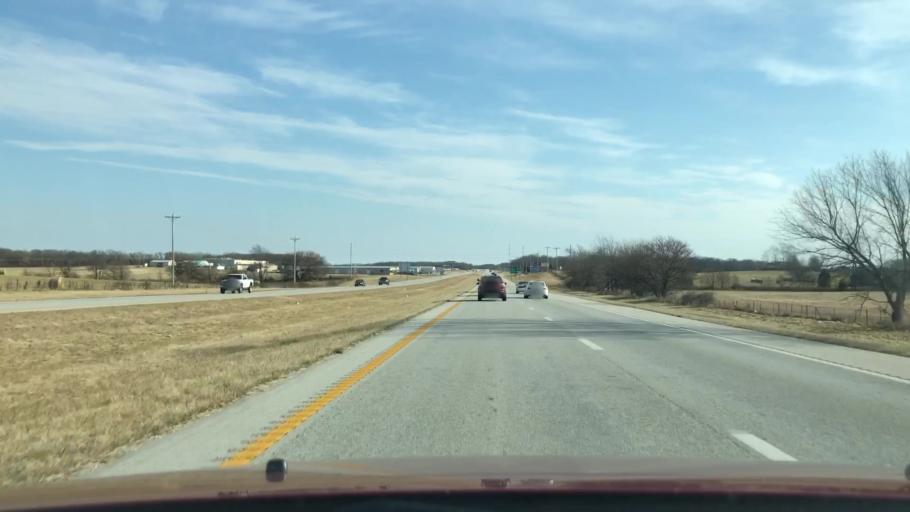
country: US
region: Missouri
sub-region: Webster County
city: Rogersville
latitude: 37.1124
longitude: -93.0463
